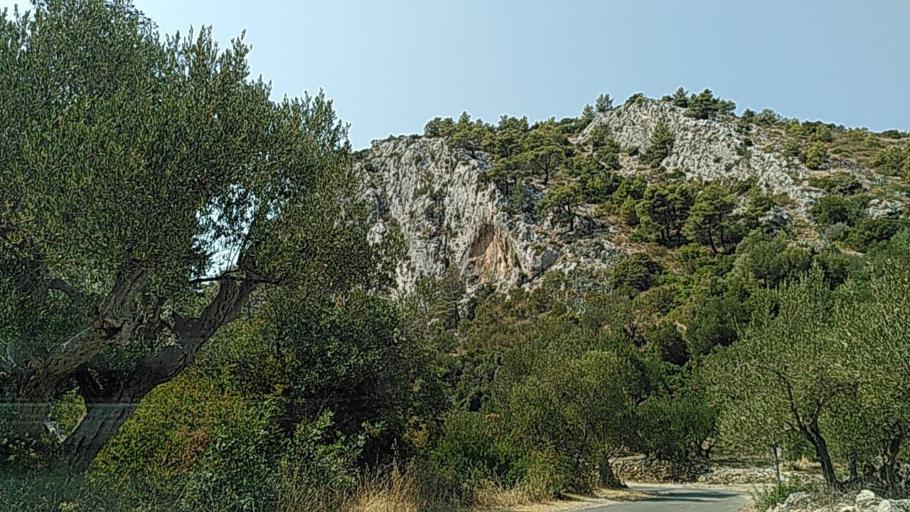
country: HR
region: Splitsko-Dalmatinska
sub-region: Grad Hvar
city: Hvar
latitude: 43.1679
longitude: 16.5031
